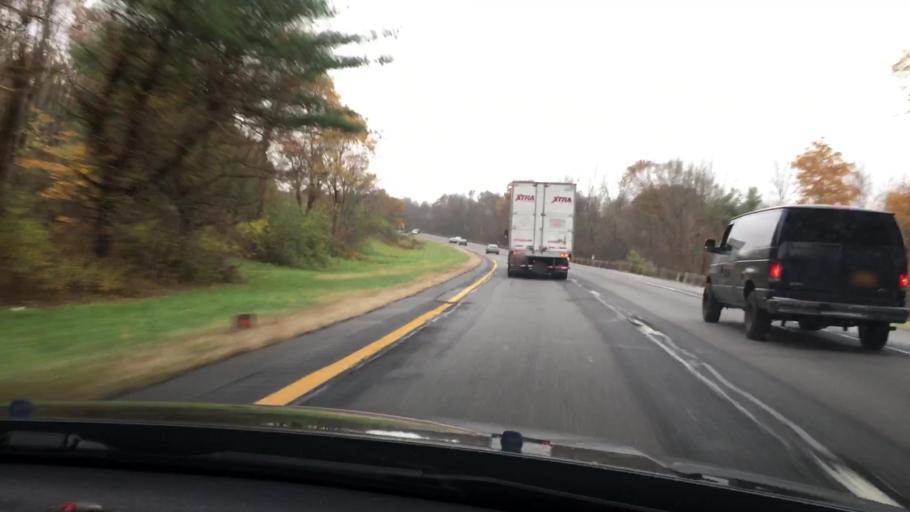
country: US
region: New York
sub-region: Putnam County
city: Lake Carmel
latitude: 41.4972
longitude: -73.6678
